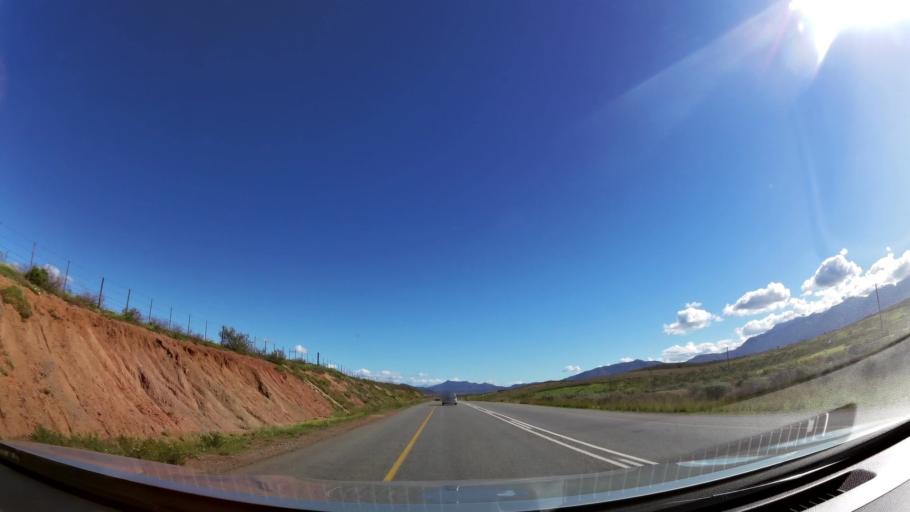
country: ZA
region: Western Cape
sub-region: Cape Winelands District Municipality
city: Ashton
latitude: -33.8180
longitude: 19.9595
